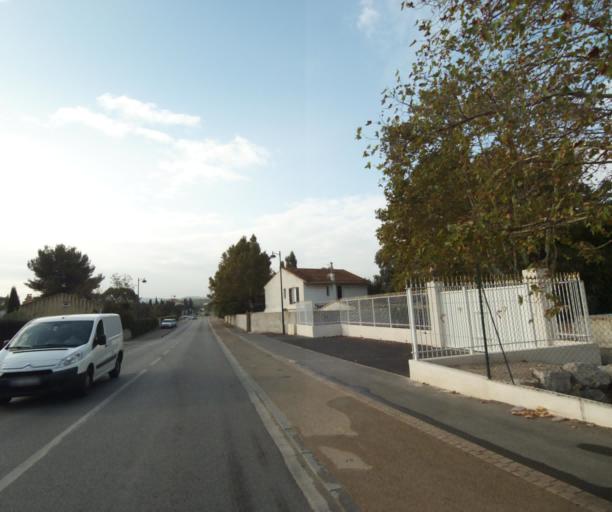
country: FR
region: Provence-Alpes-Cote d'Azur
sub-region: Departement des Bouches-du-Rhone
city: Saint-Victoret
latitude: 43.4207
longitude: 5.2446
